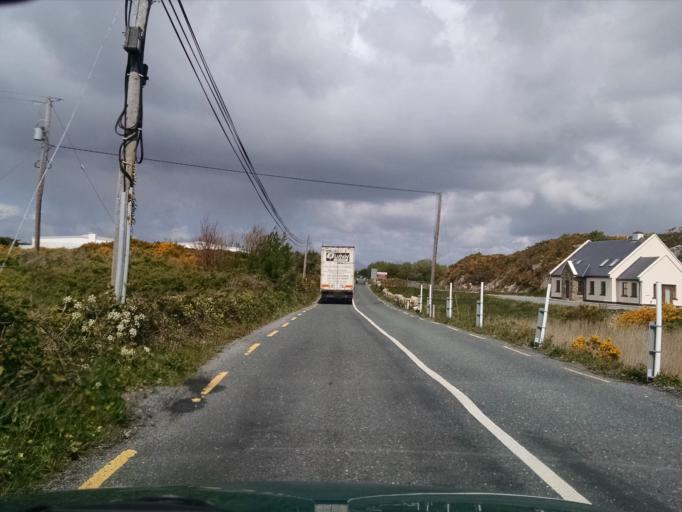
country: IE
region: Connaught
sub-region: County Galway
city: Oughterard
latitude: 53.2892
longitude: -9.5488
